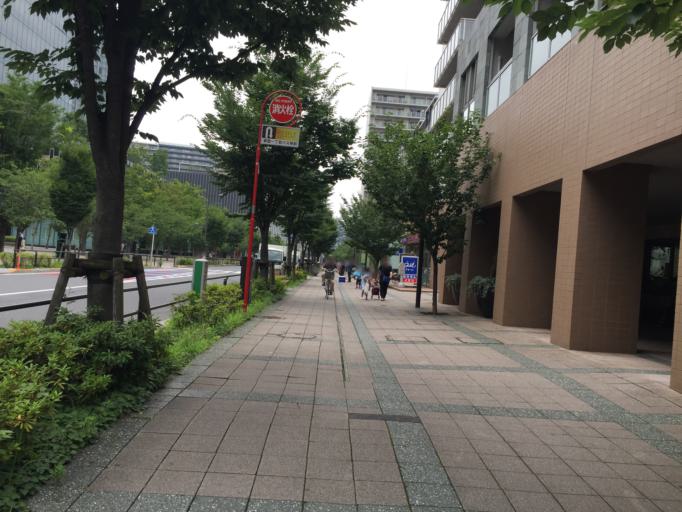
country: JP
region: Tokyo
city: Urayasu
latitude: 35.6582
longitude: 139.7958
